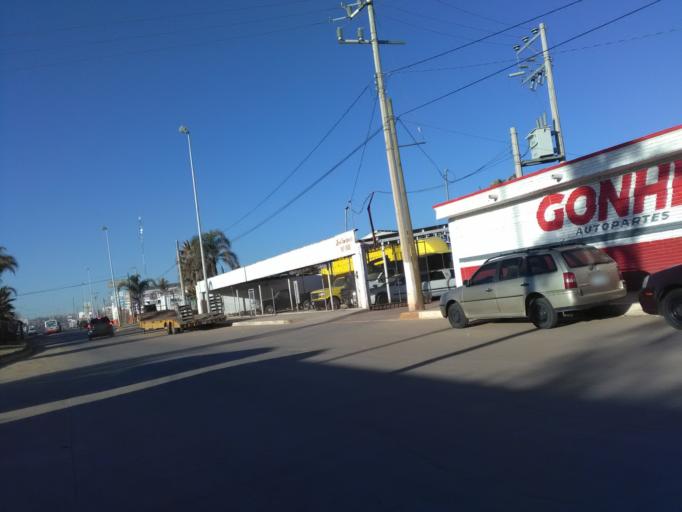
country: MX
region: Durango
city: Victoria de Durango
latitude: 24.0526
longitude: -104.6449
